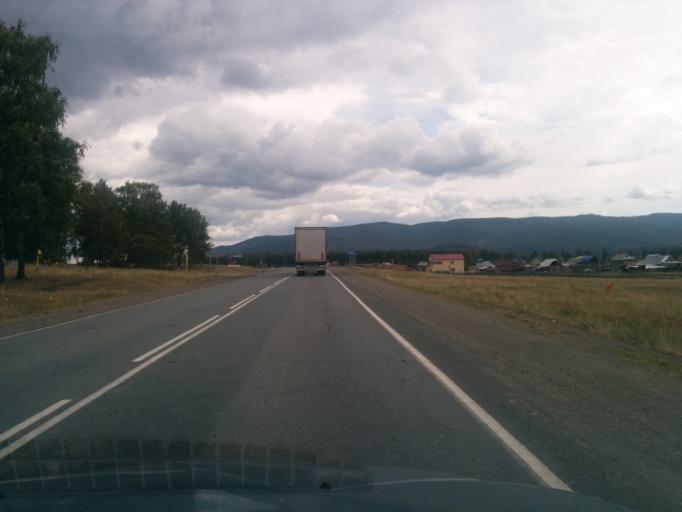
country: RU
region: Bashkortostan
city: Lomovka
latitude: 53.8851
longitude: 58.0992
